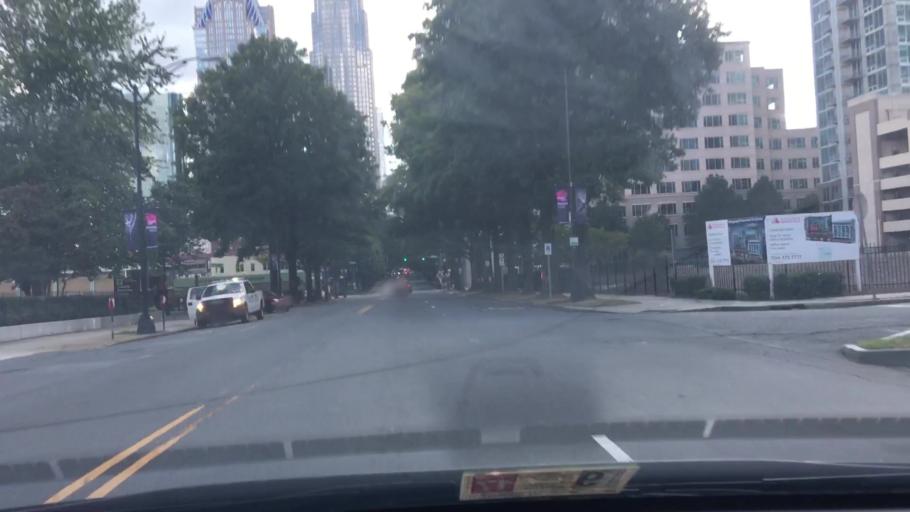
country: US
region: North Carolina
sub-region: Mecklenburg County
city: Charlotte
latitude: 35.2320
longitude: -80.8364
